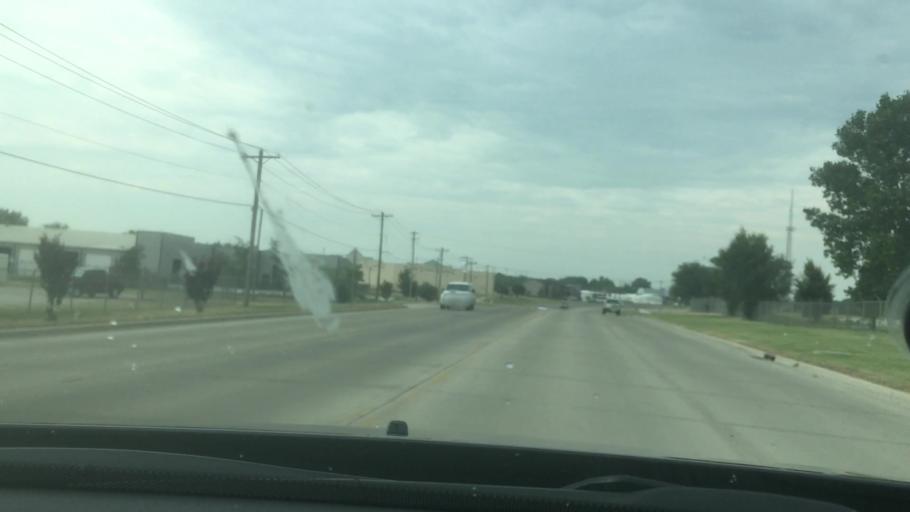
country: US
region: Oklahoma
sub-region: Pontotoc County
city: Ada
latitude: 34.7696
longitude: -96.6993
